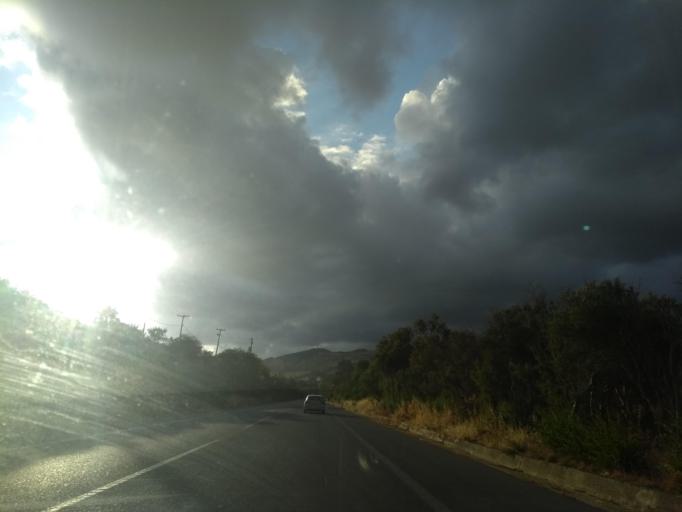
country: GR
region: Crete
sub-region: Nomos Rethymnis
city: Panormos
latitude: 35.4140
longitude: 24.7134
